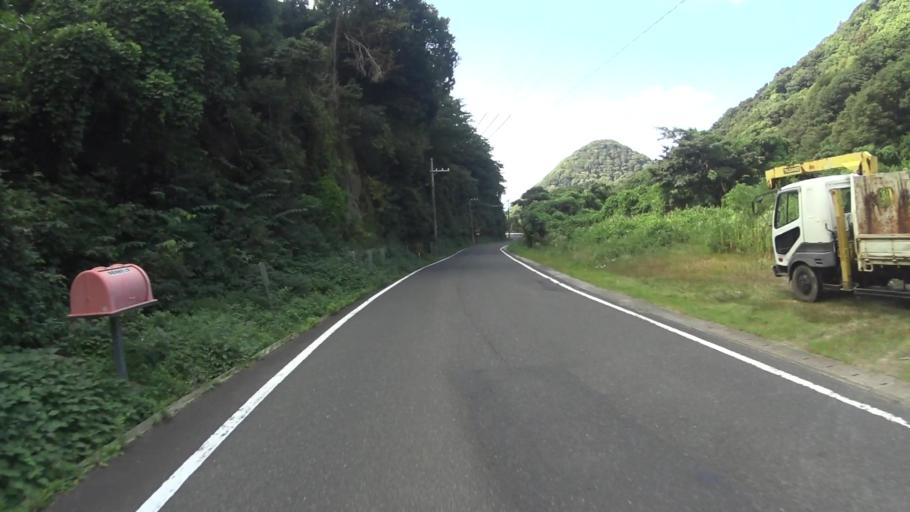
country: JP
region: Kyoto
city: Miyazu
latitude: 35.7677
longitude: 135.2279
